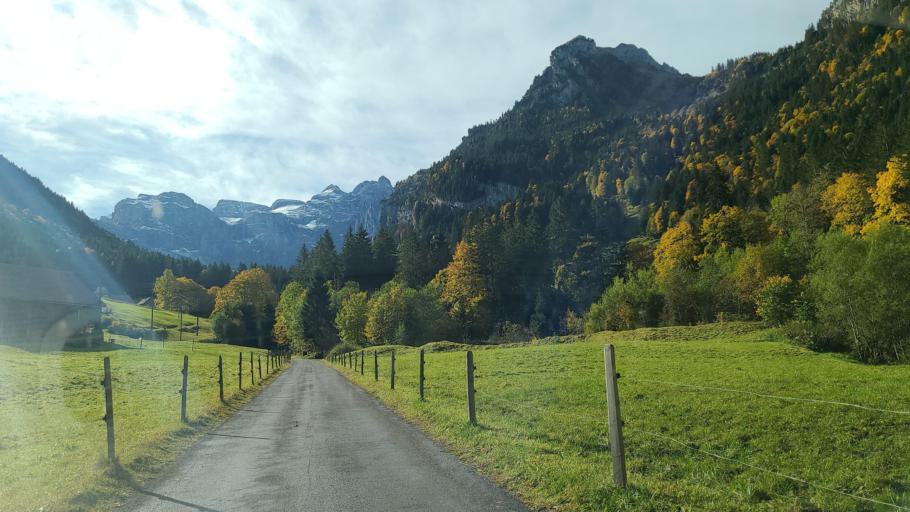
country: CH
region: Nidwalden
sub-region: Nidwalden
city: Emmetten
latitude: 46.9010
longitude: 8.5224
